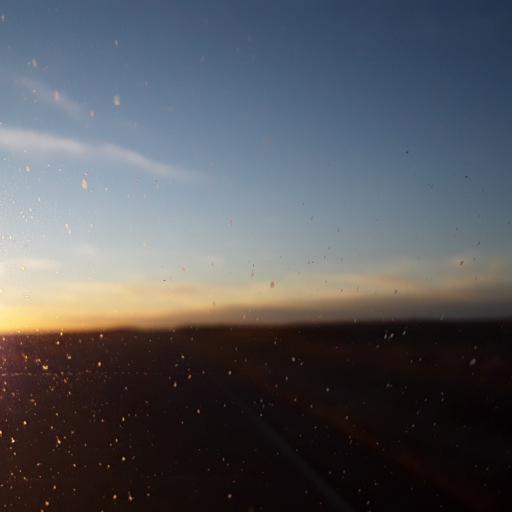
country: US
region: Colorado
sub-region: Kiowa County
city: Eads
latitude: 38.7785
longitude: -102.7286
